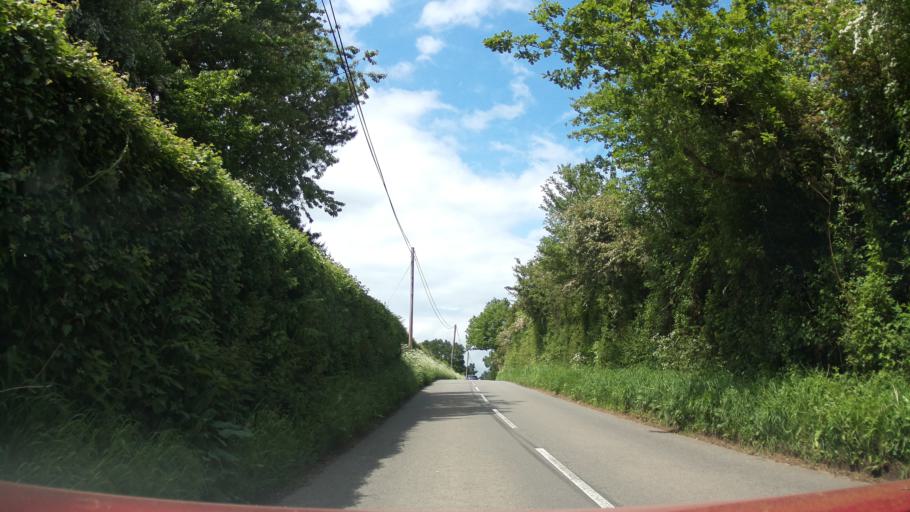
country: GB
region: England
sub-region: Herefordshire
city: Llanrothal
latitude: 51.8550
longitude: -2.8054
